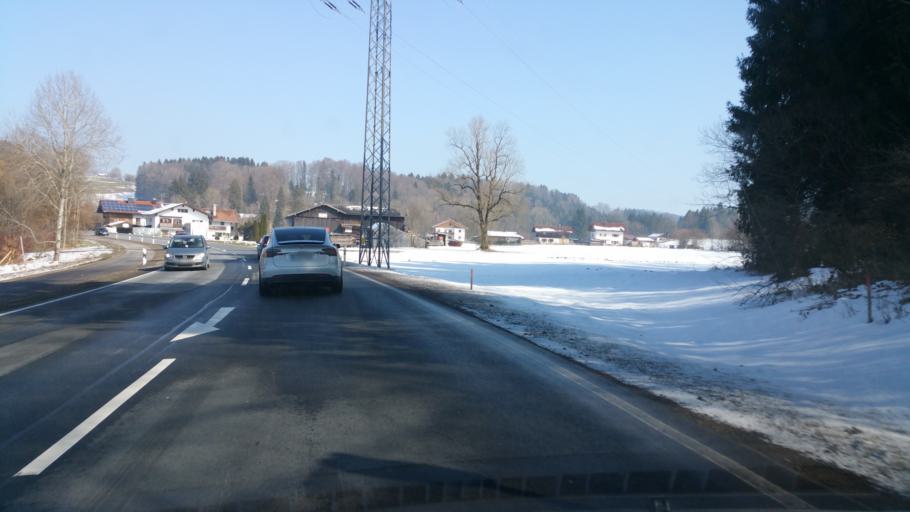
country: DE
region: Bavaria
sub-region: Upper Bavaria
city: Miesbach
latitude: 47.8064
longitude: 11.8758
